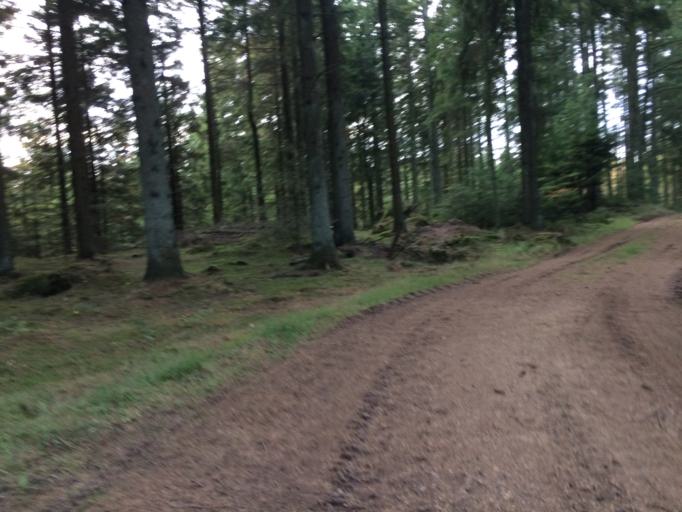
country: DK
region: Central Jutland
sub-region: Holstebro Kommune
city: Ulfborg
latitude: 56.2077
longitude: 8.4572
